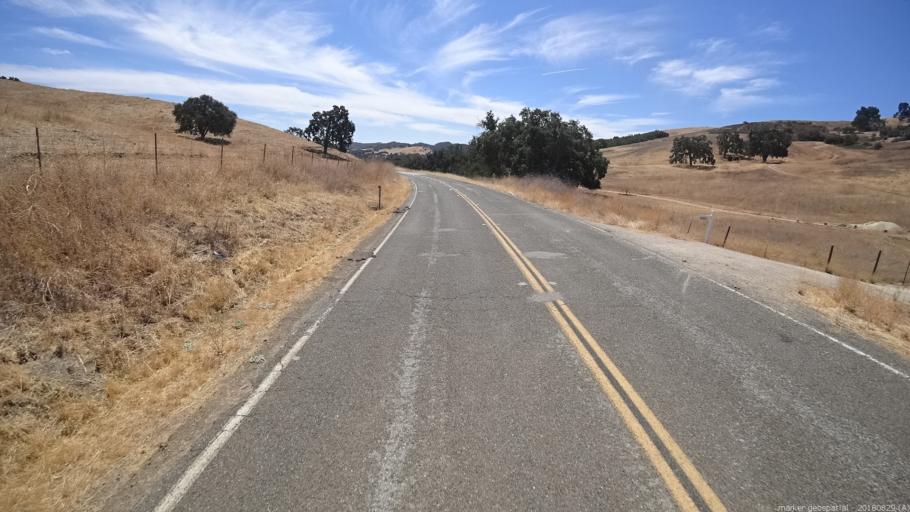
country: US
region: California
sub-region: San Luis Obispo County
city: Lake Nacimiento
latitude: 35.8470
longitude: -121.0491
